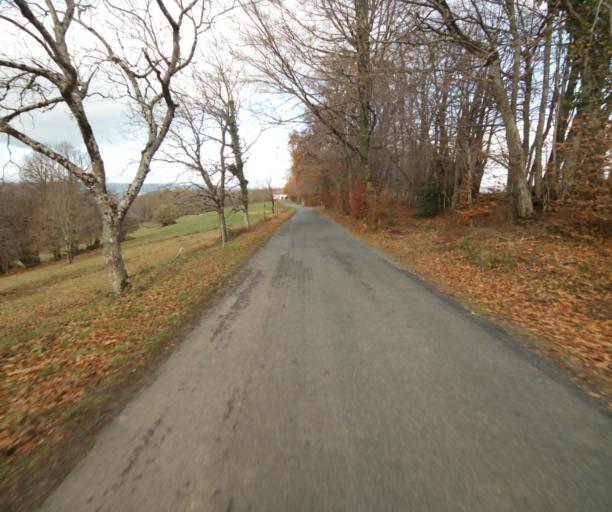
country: FR
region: Limousin
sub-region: Departement de la Correze
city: Laguenne
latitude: 45.2233
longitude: 1.7919
